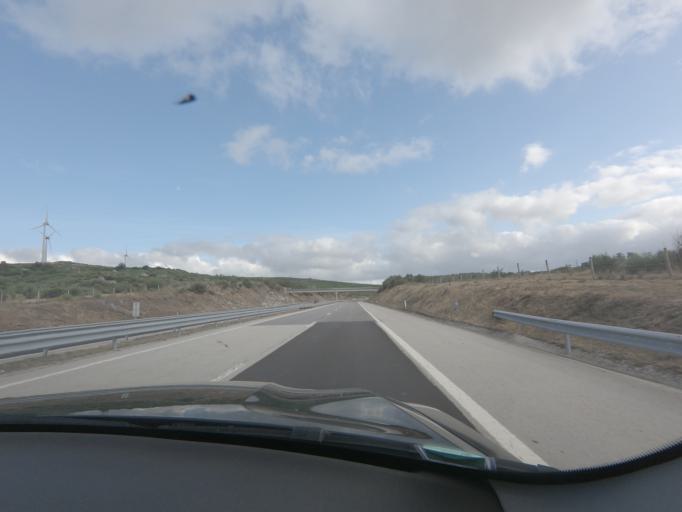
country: PT
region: Viseu
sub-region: Tarouca
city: Tarouca
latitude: 40.9985
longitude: -7.8827
